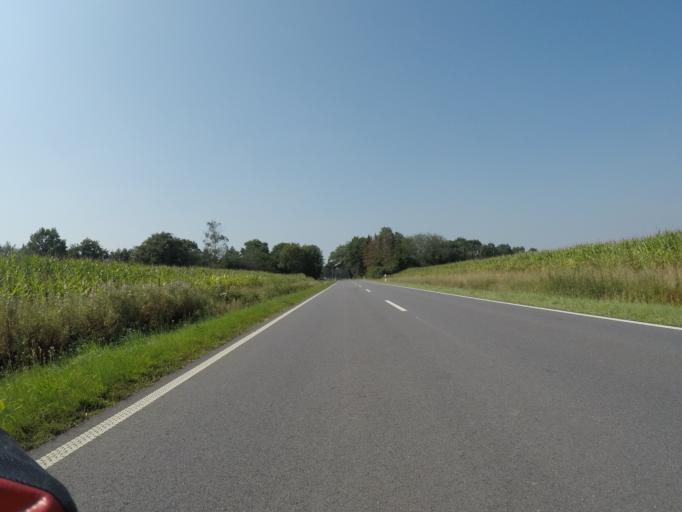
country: DE
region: Schleswig-Holstein
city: Sievershutten
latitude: 53.8421
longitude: 10.0839
